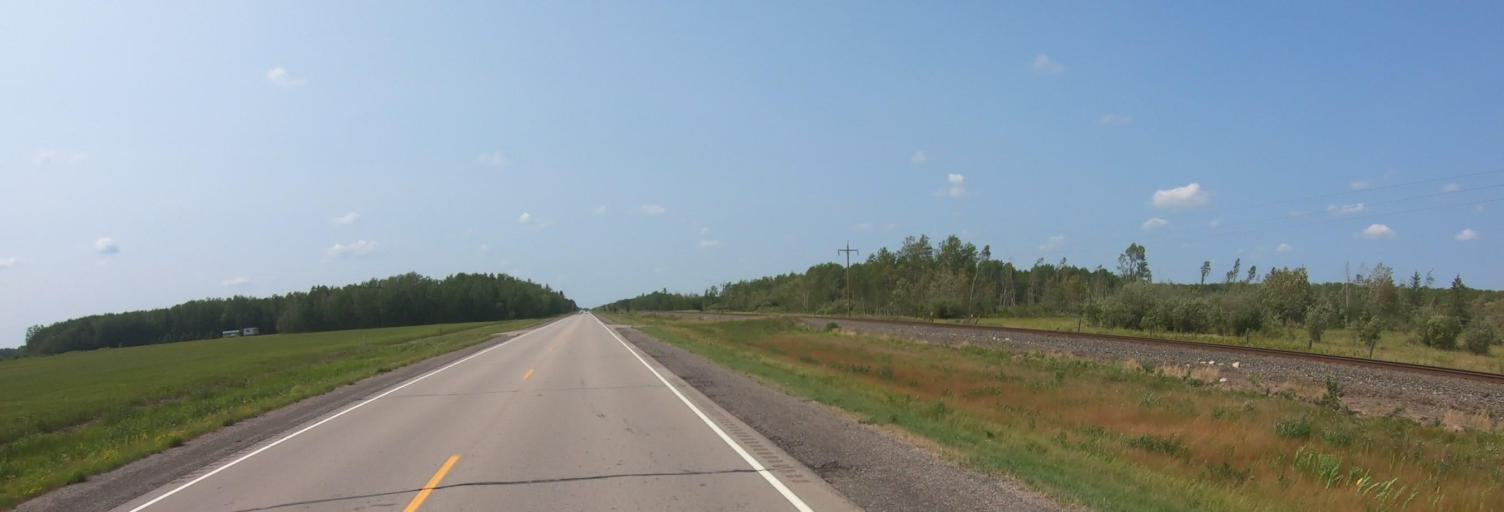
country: US
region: Minnesota
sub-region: Lake of the Woods County
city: Baudette
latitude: 48.7241
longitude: -94.7679
